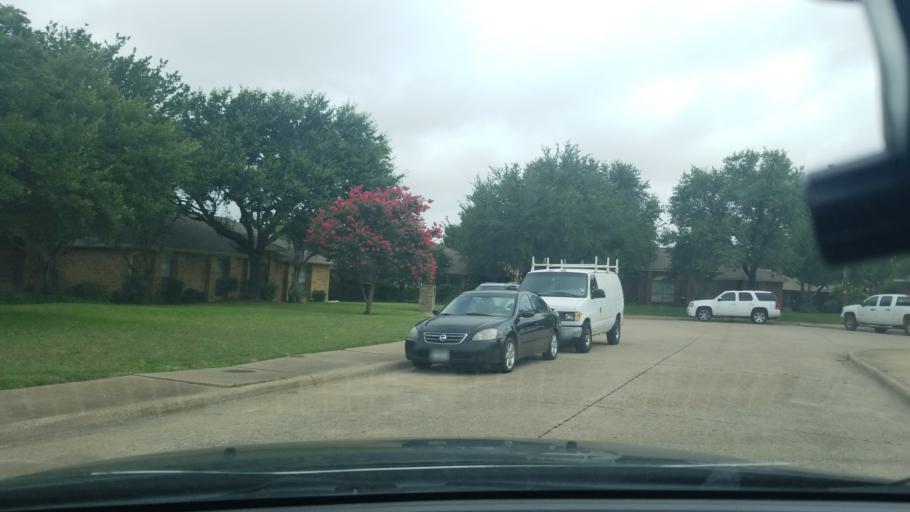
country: US
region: Texas
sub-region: Dallas County
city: Balch Springs
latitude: 32.7864
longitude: -96.6878
